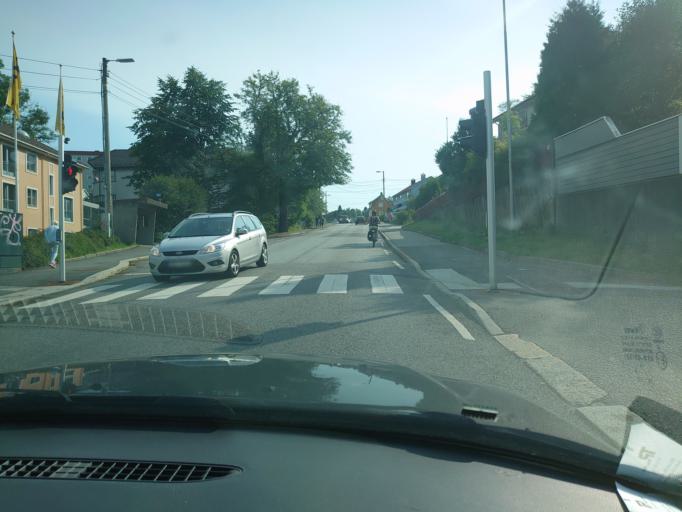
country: NO
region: Hordaland
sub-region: Bergen
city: Bergen
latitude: 60.3759
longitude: 5.3039
